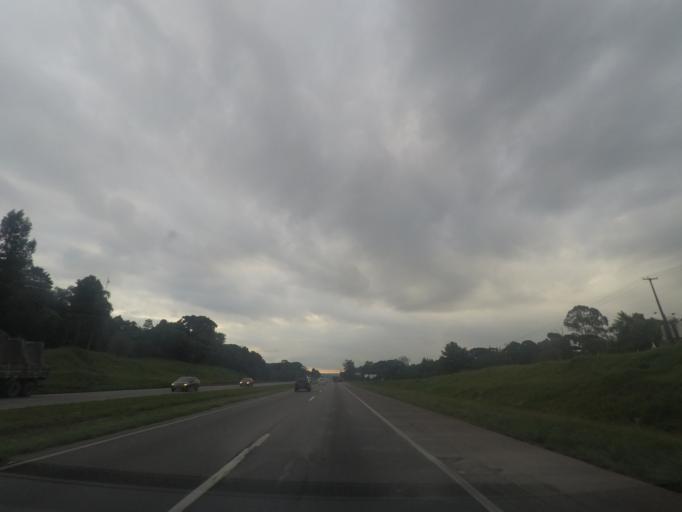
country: BR
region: Parana
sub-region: Sao Jose Dos Pinhais
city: Sao Jose dos Pinhais
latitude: -25.5718
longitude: -49.2050
